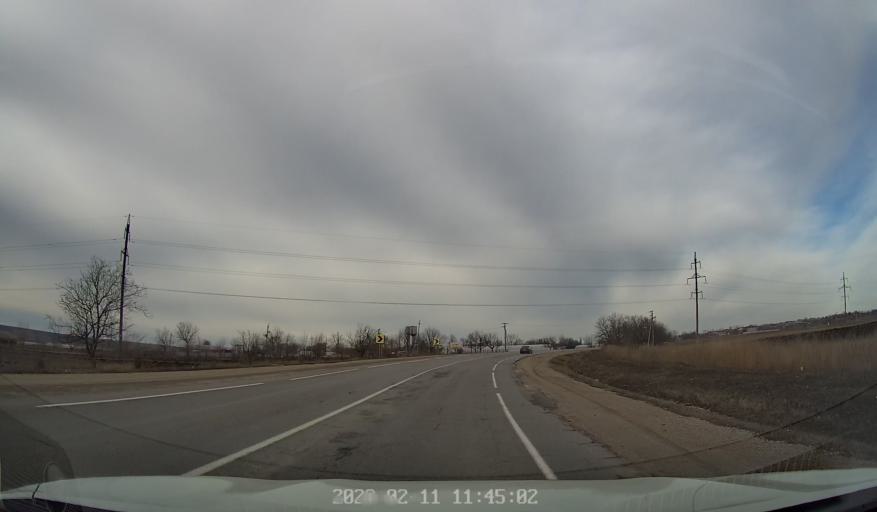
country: MD
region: Balti
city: Balti
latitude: 47.8026
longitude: 27.8442
